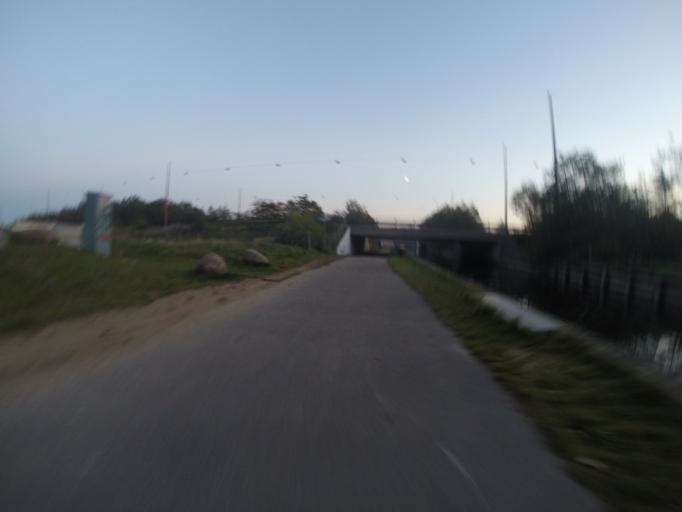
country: DK
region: Capital Region
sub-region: Vallensbaek Kommune
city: Vallensbaek
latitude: 55.6418
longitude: 12.3506
